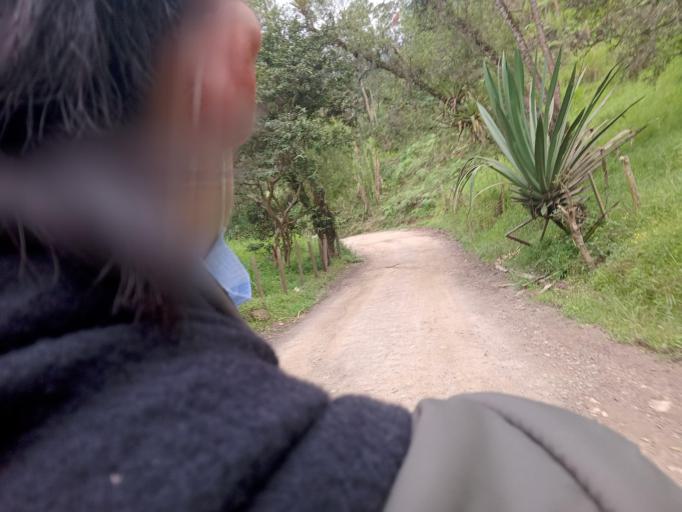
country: CO
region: Cundinamarca
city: Tenza
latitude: 5.1062
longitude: -73.4428
